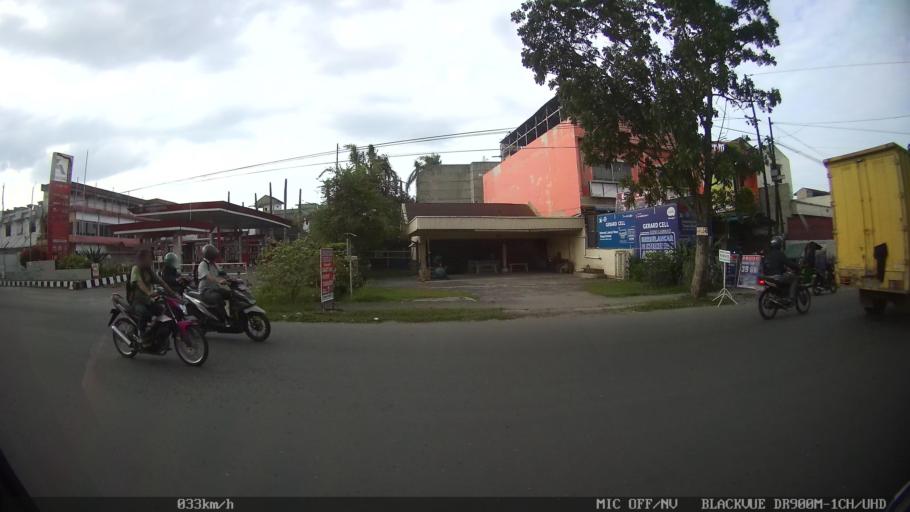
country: ID
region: North Sumatra
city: Sunggal
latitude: 3.5409
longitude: 98.6248
